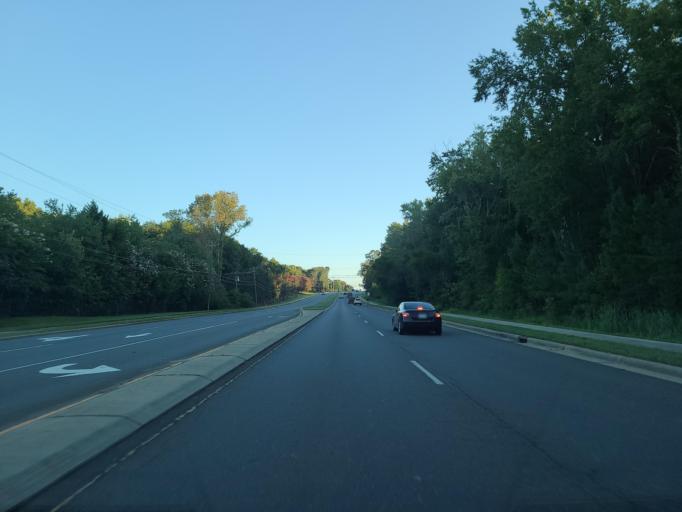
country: US
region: North Carolina
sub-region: Union County
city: Weddington
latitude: 35.0428
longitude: -80.7688
